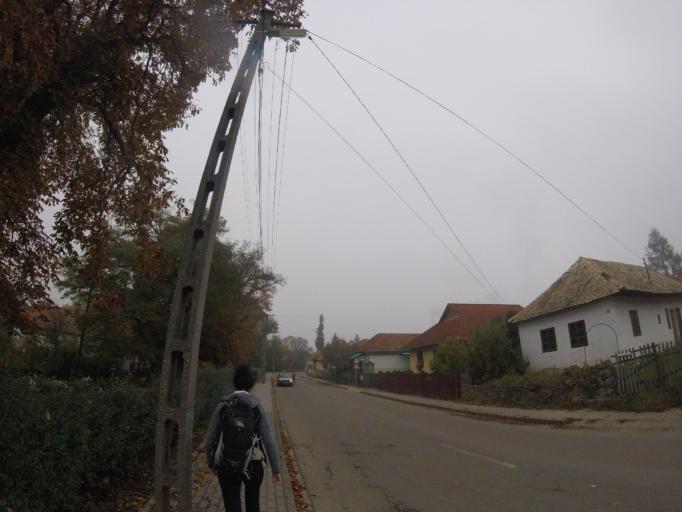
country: HU
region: Heves
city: Szilvasvarad
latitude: 48.1755
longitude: 20.4869
